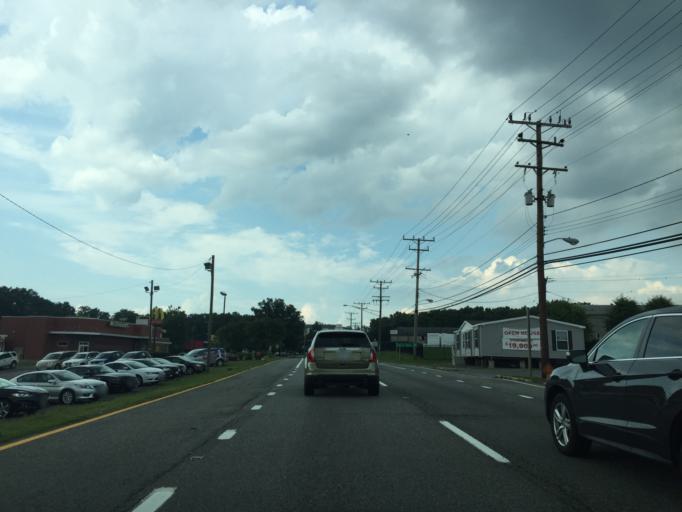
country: US
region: Maryland
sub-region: Prince George's County
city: Laurel
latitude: 39.1096
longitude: -76.8365
